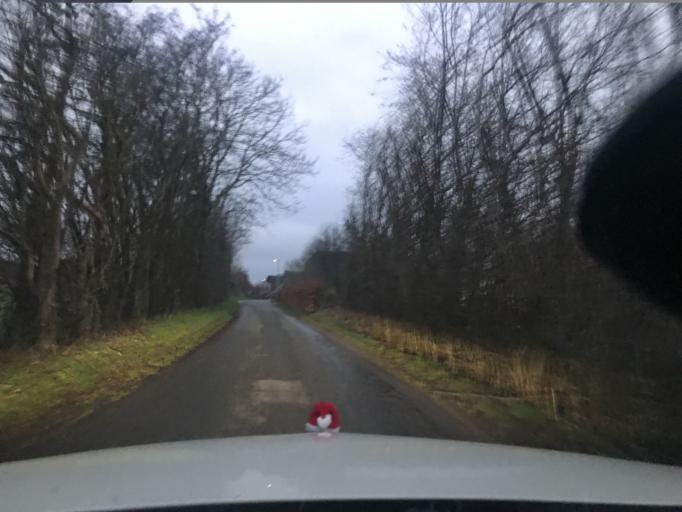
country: DK
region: South Denmark
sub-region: Sonderborg Kommune
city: Dybbol
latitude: 54.8589
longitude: 9.7257
